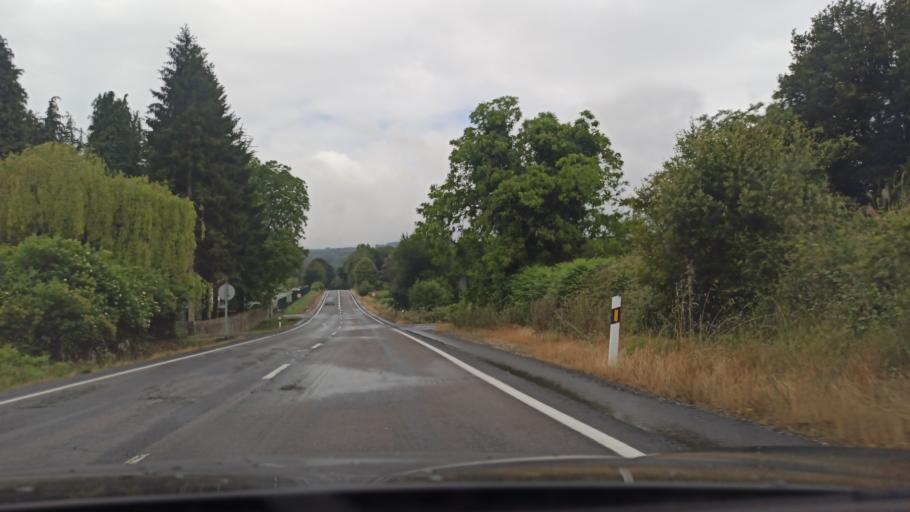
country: ES
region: Galicia
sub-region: Provincia de Lugo
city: Monterroso
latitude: 42.7818
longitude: -7.9030
